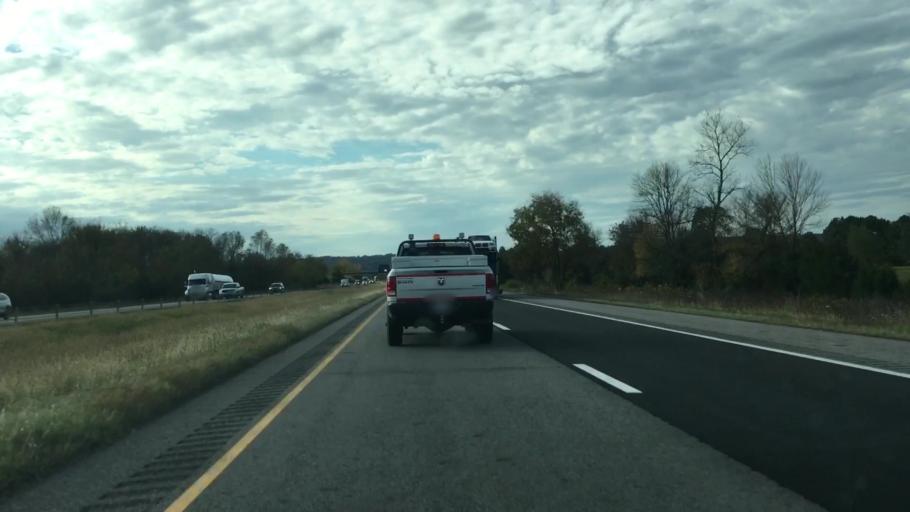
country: US
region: Arkansas
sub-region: Pope County
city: Atkins
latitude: 35.2498
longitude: -92.8835
